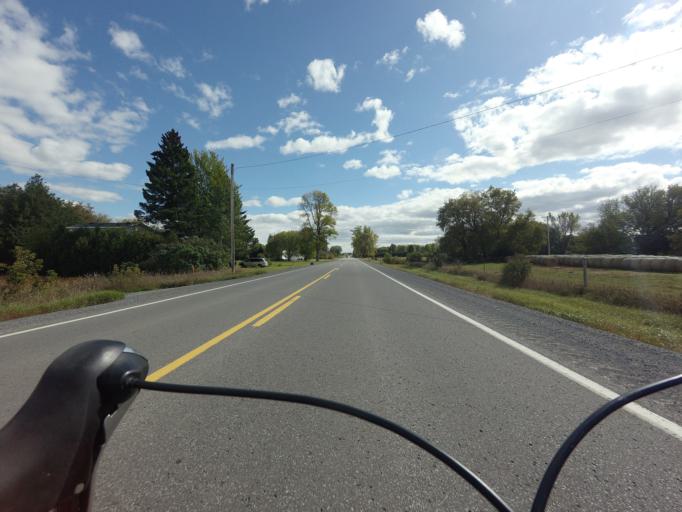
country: CA
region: Ontario
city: Bells Corners
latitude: 45.1872
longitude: -75.6771
